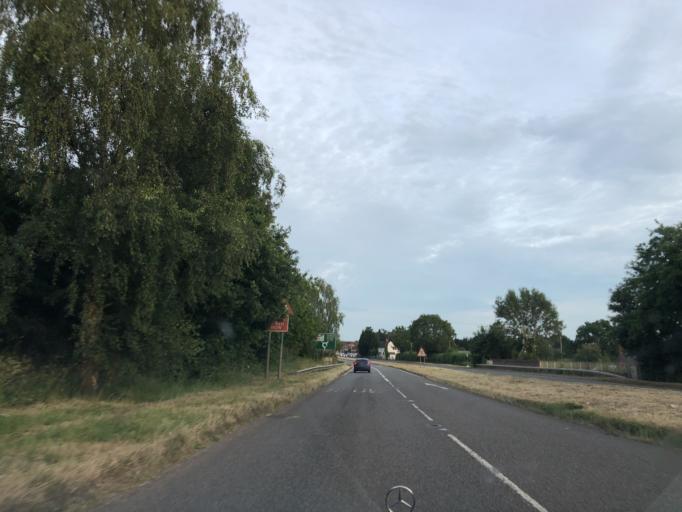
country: GB
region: England
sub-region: Solihull
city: Balsall Common
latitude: 52.4043
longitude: -1.6592
